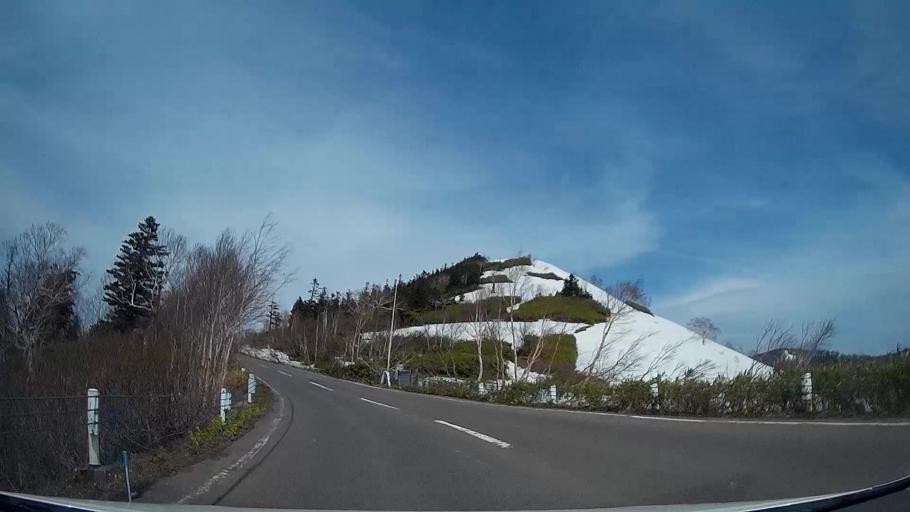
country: JP
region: Iwate
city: Shizukuishi
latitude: 39.9443
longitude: 140.9075
